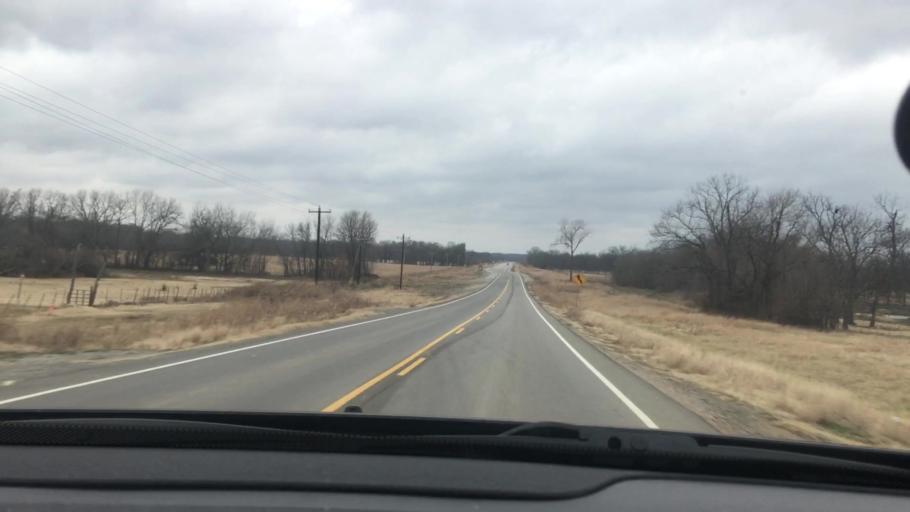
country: US
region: Oklahoma
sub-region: Atoka County
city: Atoka
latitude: 34.3749
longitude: -96.3026
